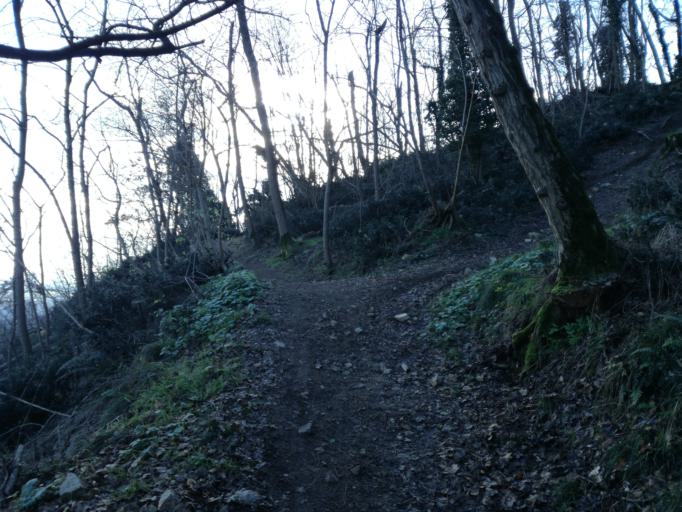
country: IT
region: Veneto
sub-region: Provincia di Padova
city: Galzignano
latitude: 45.3005
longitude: 11.7276
